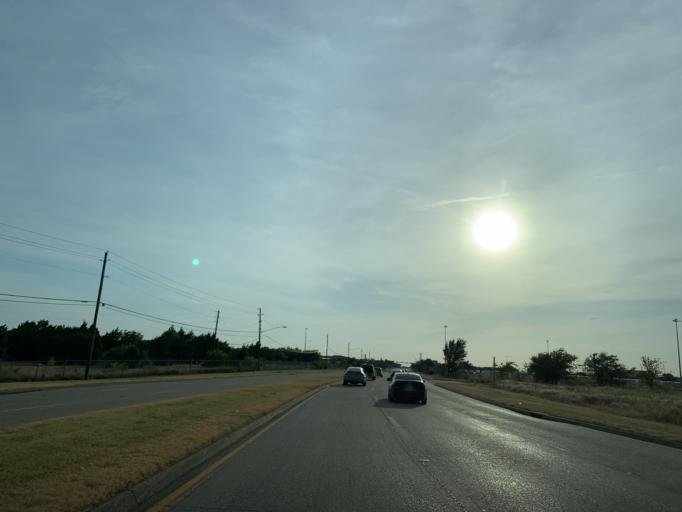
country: US
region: Texas
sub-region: Dallas County
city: Cockrell Hill
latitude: 32.7058
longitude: -96.9048
